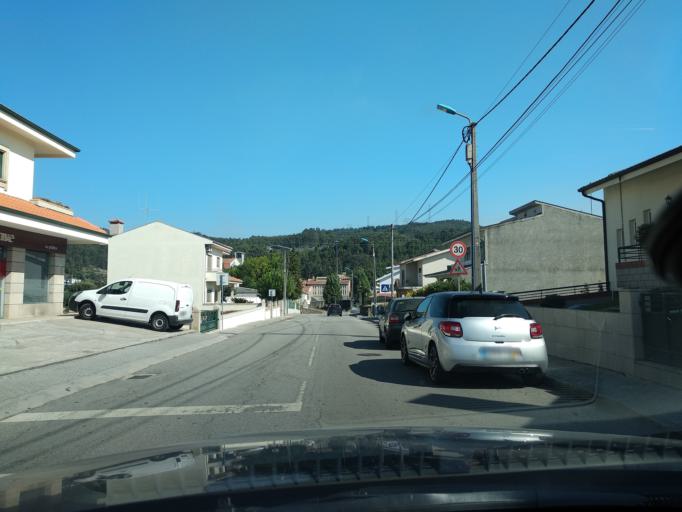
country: PT
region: Porto
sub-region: Paredes
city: Rebordosa
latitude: 41.2220
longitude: -8.4146
